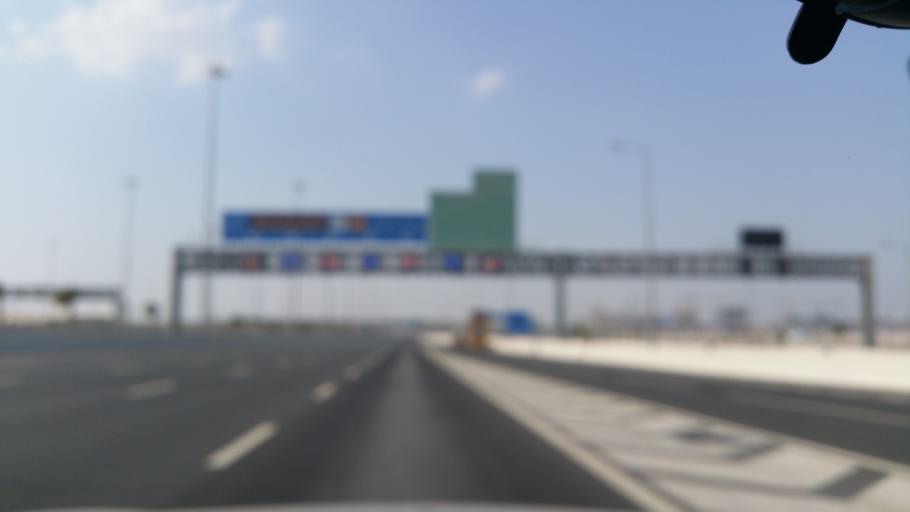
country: QA
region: Baladiyat Umm Salal
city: Umm Salal Muhammad
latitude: 25.3988
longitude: 51.4947
